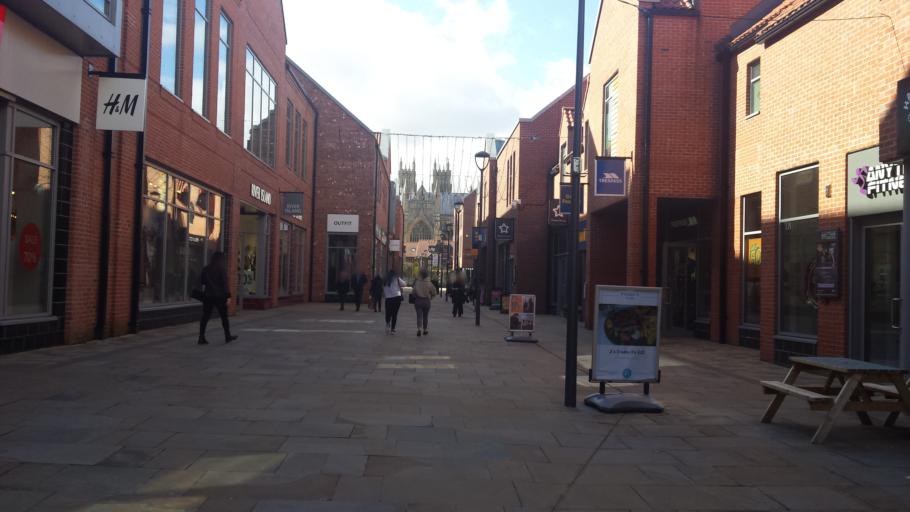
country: GB
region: England
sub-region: East Riding of Yorkshire
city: Beverley
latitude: 53.8399
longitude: -0.4199
